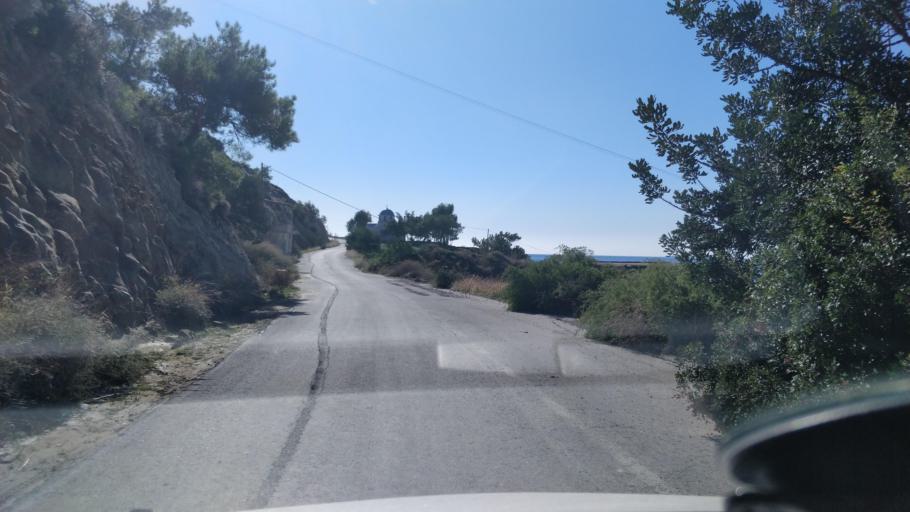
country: GR
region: Crete
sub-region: Nomos Lasithiou
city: Gra Liyia
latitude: 34.9880
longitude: 25.4835
